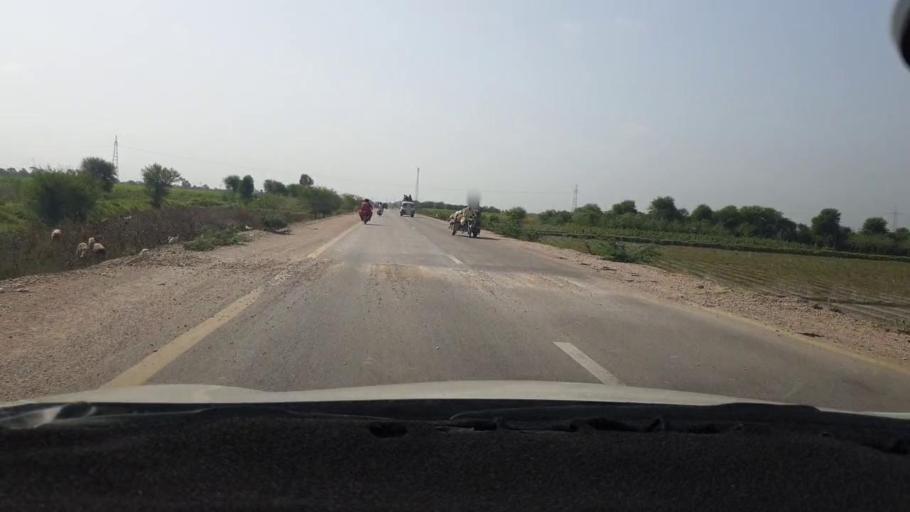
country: PK
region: Sindh
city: Tando Mittha Khan
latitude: 25.8349
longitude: 69.0631
